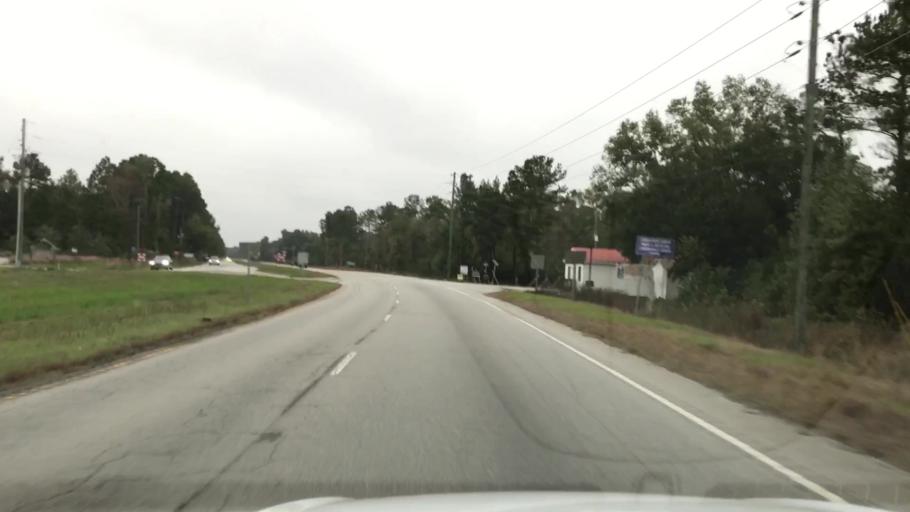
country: US
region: South Carolina
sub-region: Charleston County
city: Awendaw
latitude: 32.9898
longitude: -79.6462
